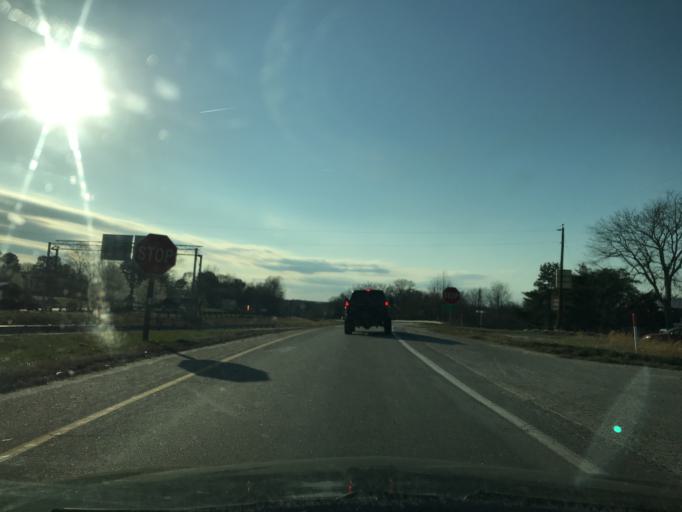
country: US
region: Virginia
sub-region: Prince Edward County
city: Farmville
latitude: 37.2734
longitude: -78.2861
